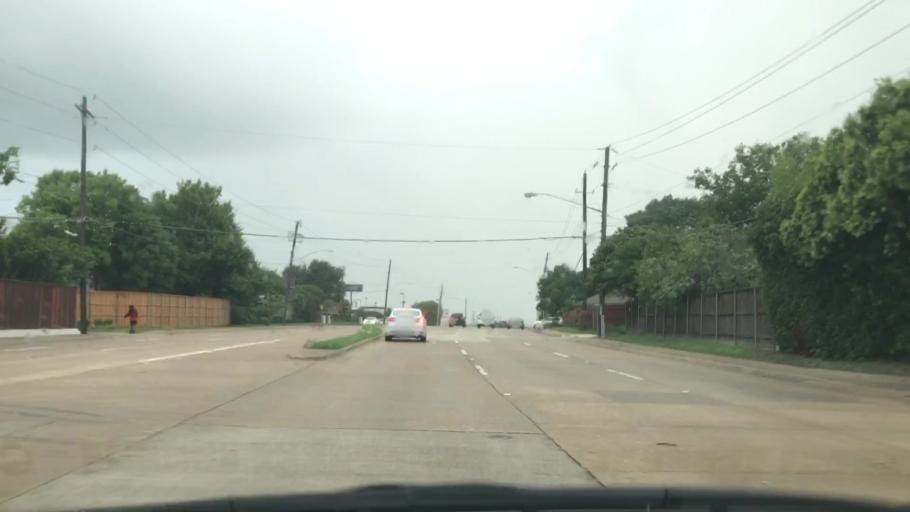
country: US
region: Texas
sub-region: Dallas County
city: Richardson
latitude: 32.8969
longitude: -96.7392
